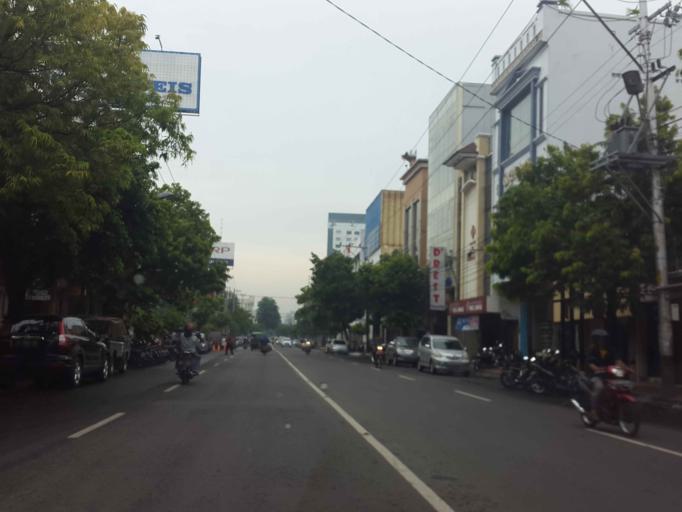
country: ID
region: Central Java
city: Semarang
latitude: -6.9743
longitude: 110.4201
